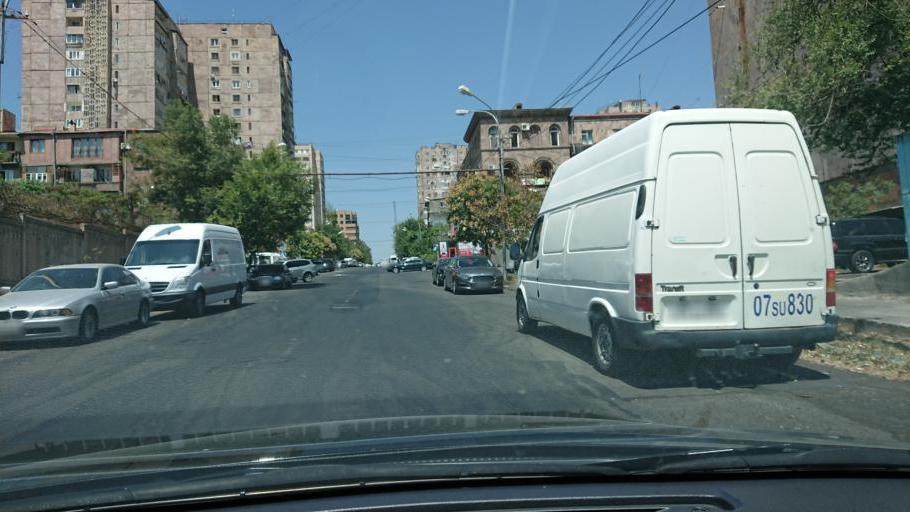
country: AM
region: Yerevan
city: Yerevan
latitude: 40.1963
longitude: 44.5032
